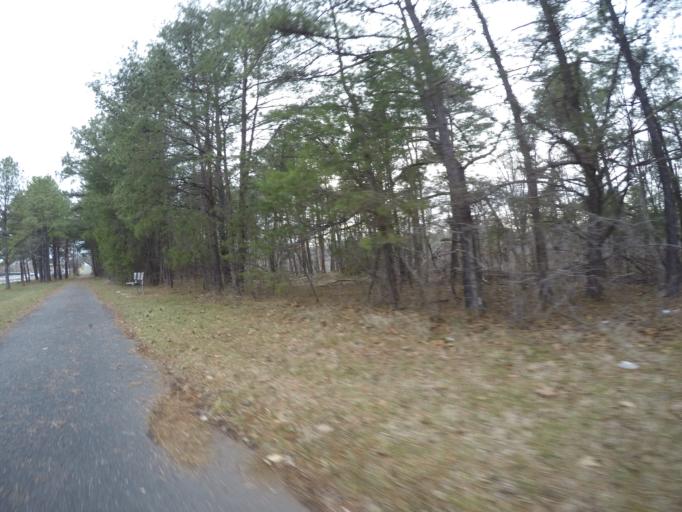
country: US
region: Maryland
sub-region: Howard County
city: Hanover
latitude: 39.1812
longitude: -76.6924
